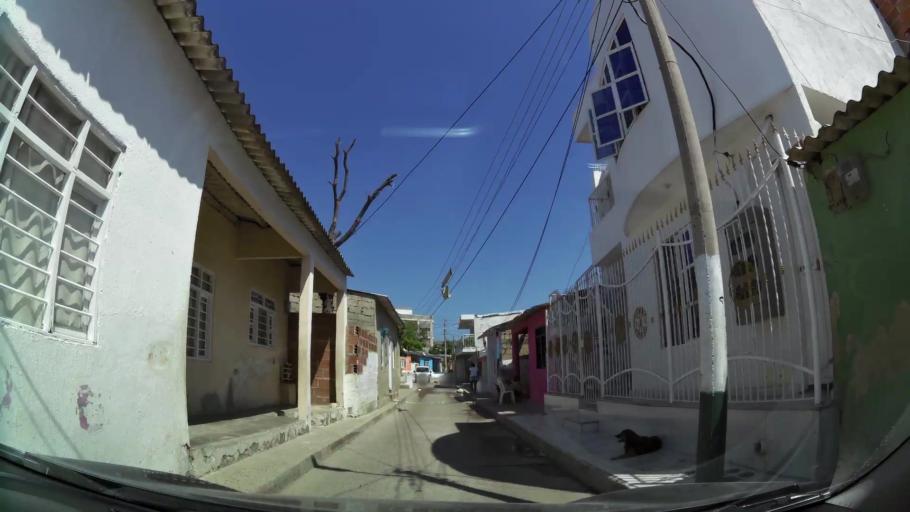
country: CO
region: Bolivar
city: Cartagena
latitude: 10.3861
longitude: -75.5083
